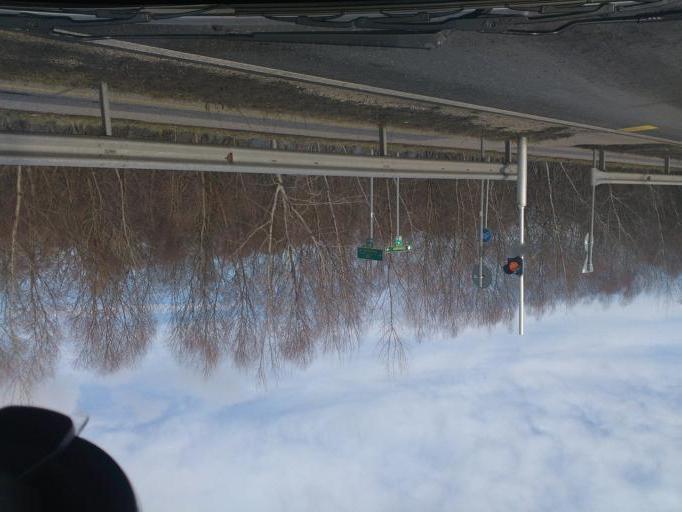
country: HU
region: Komarom-Esztergom
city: Tat
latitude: 47.7499
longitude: 18.6313
